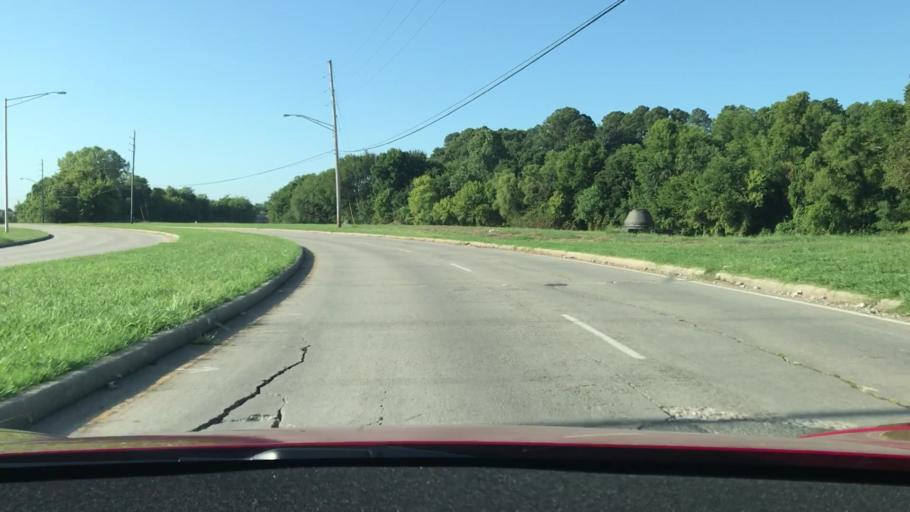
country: US
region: Louisiana
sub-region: Bossier Parish
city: Bossier City
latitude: 32.4366
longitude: -93.7286
